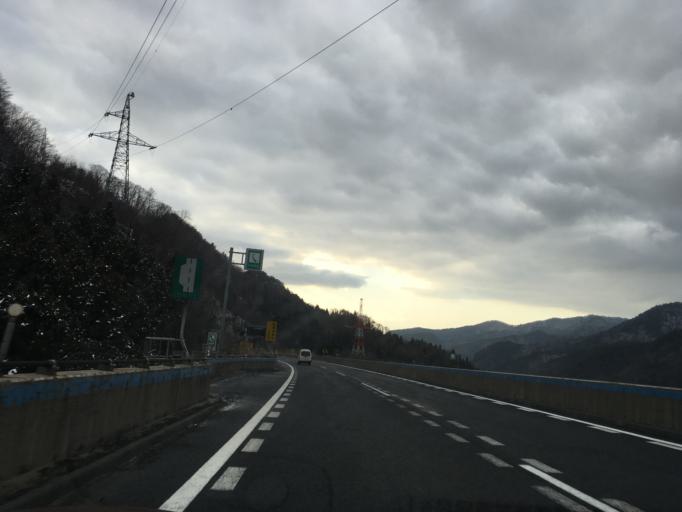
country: JP
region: Yamagata
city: Yamagata-shi
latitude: 38.2247
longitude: 140.4235
